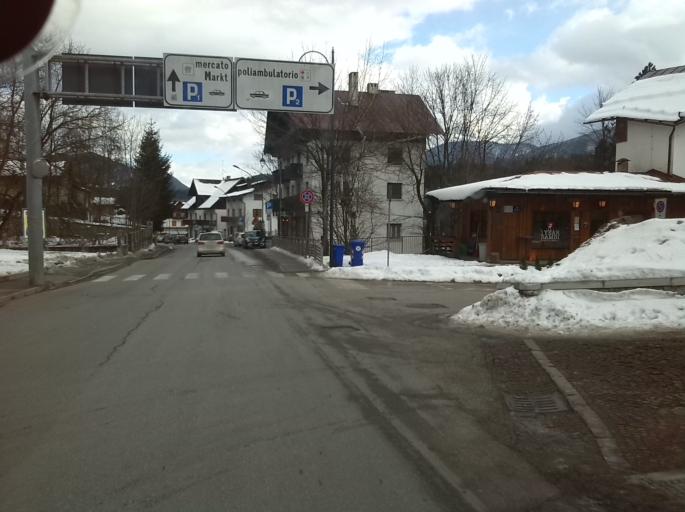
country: IT
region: Friuli Venezia Giulia
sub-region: Provincia di Udine
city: Tarvisio
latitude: 46.5045
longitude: 13.5770
